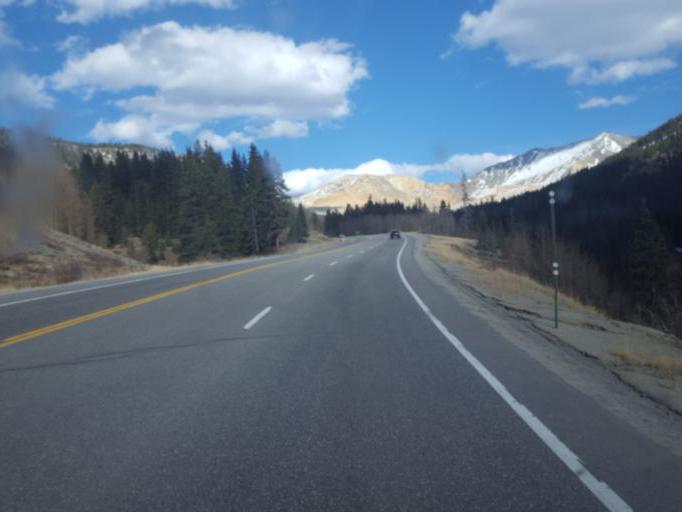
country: US
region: Colorado
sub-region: Lake County
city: Leadville
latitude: 39.3542
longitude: -106.2156
